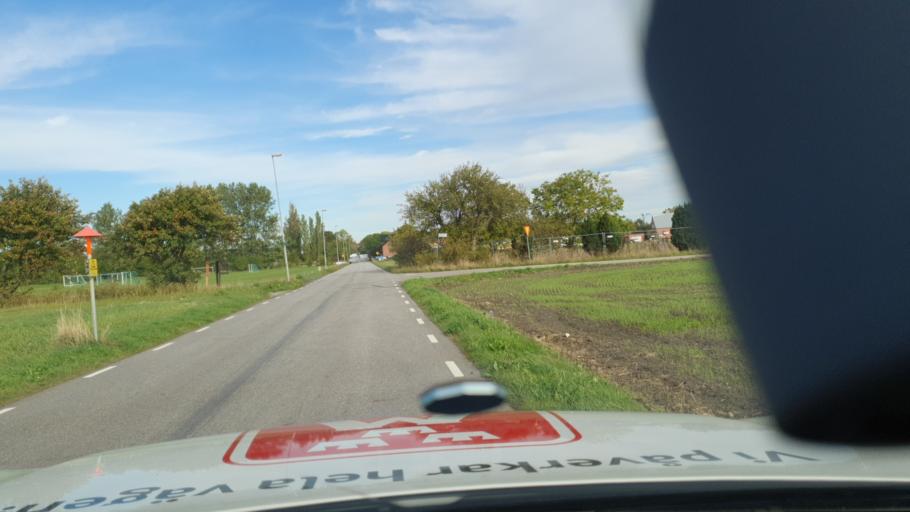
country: SE
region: Skane
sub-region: Malmo
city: Bunkeflostrand
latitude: 55.5186
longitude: 12.9340
